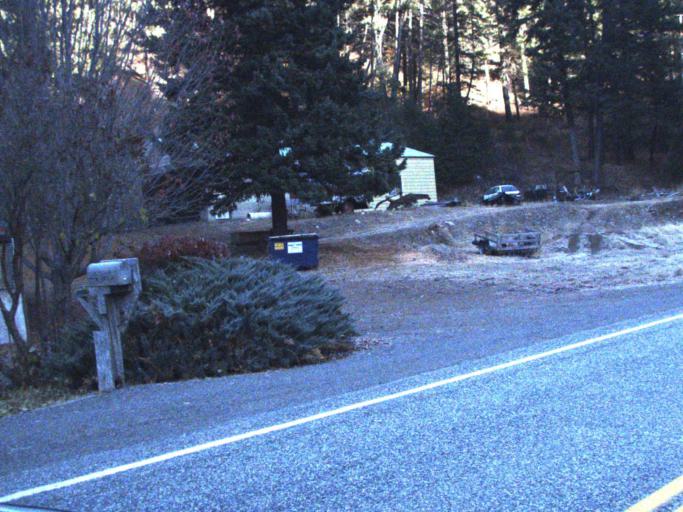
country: US
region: Washington
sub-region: Ferry County
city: Republic
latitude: 48.5495
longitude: -118.7488
